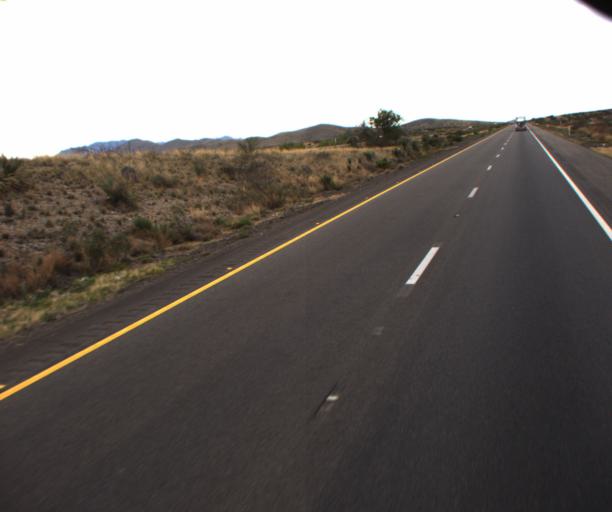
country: US
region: Arizona
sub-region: Cochise County
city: Willcox
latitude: 32.1335
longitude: -110.0069
